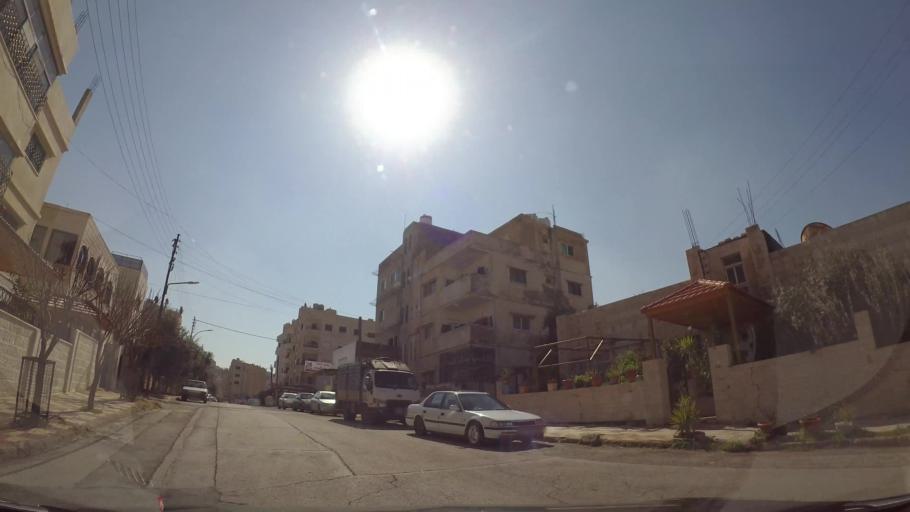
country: JO
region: Amman
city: Amman
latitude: 31.9852
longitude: 35.9797
